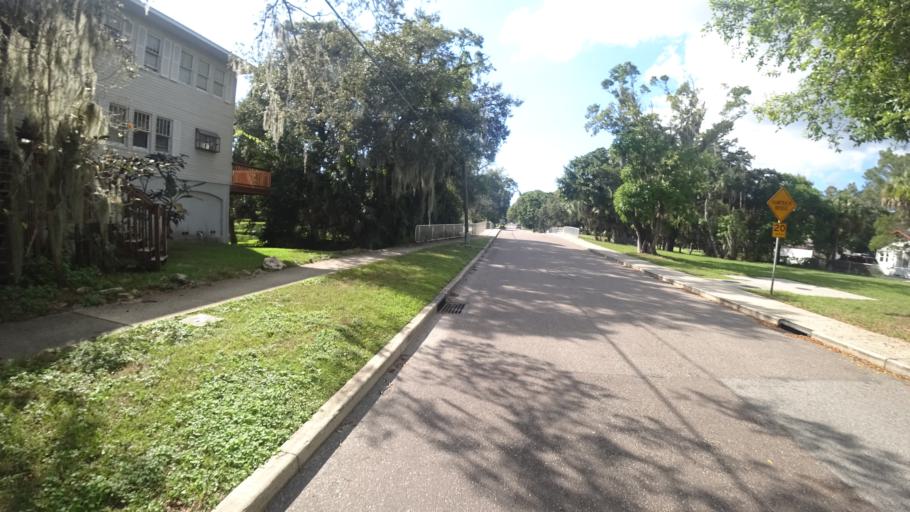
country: US
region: Florida
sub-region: Manatee County
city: Bradenton
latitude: 27.4891
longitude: -82.5815
